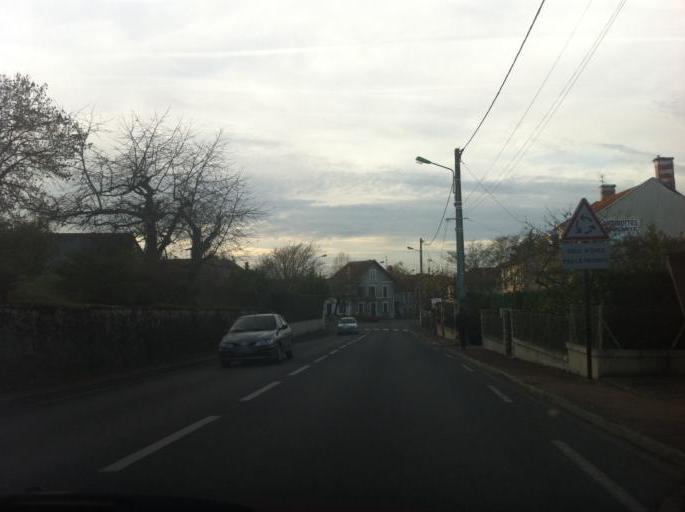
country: FR
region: Aquitaine
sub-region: Departement de la Dordogne
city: Tocane-Saint-Apre
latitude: 45.2482
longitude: 0.4466
